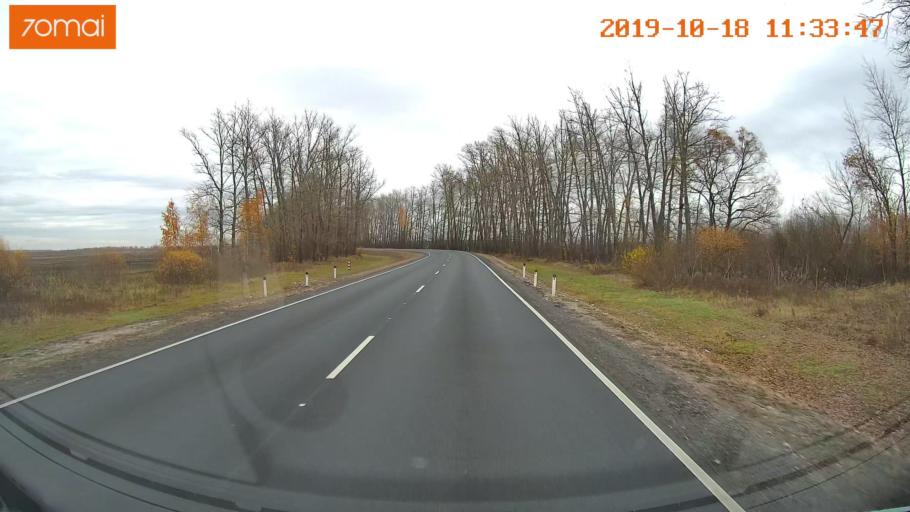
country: RU
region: Rjazan
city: Oktyabr'skiy
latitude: 54.1383
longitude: 38.7489
